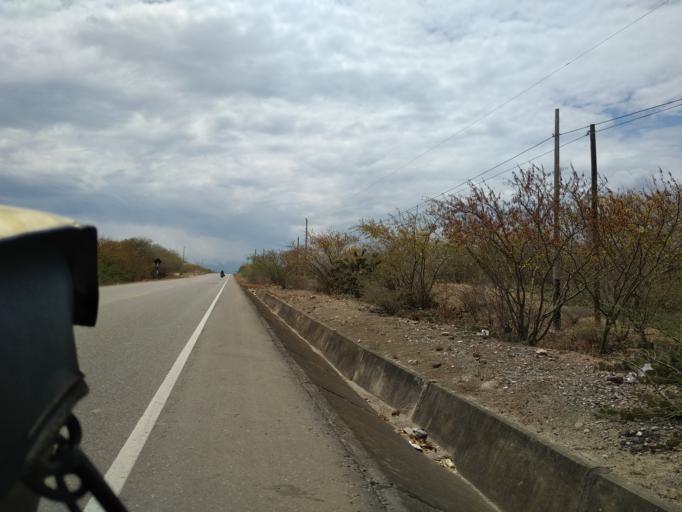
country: PE
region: Cajamarca
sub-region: Provincia de Jaen
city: Bellavista
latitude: -5.7365
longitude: -78.6456
